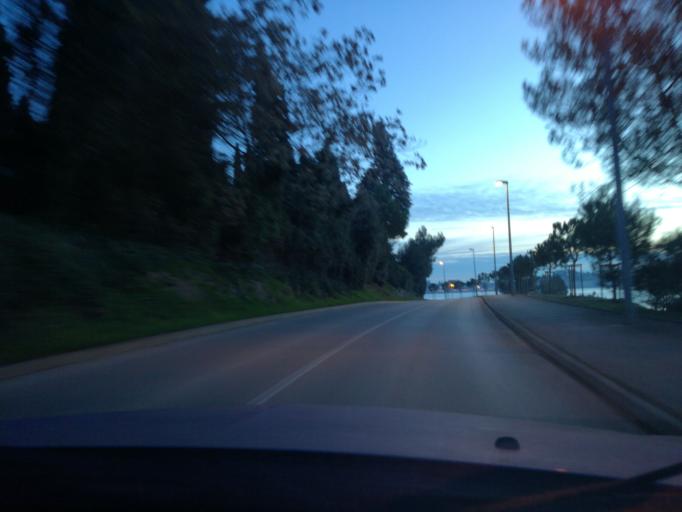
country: HR
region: Istarska
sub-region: Grad Rovinj
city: Rovinj
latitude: 45.0967
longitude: 13.6416
